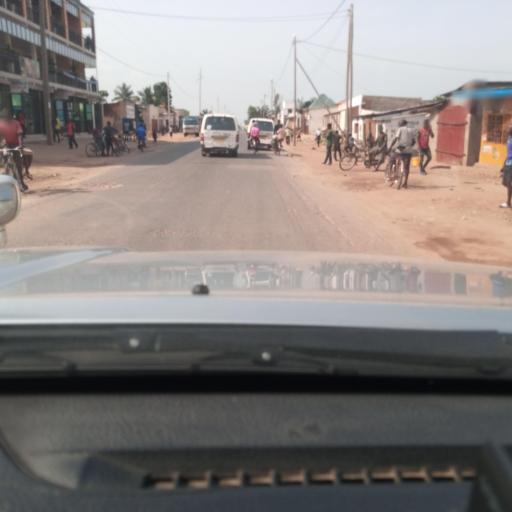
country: BI
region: Bujumbura Mairie
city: Bujumbura
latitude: -3.4530
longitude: 29.3518
